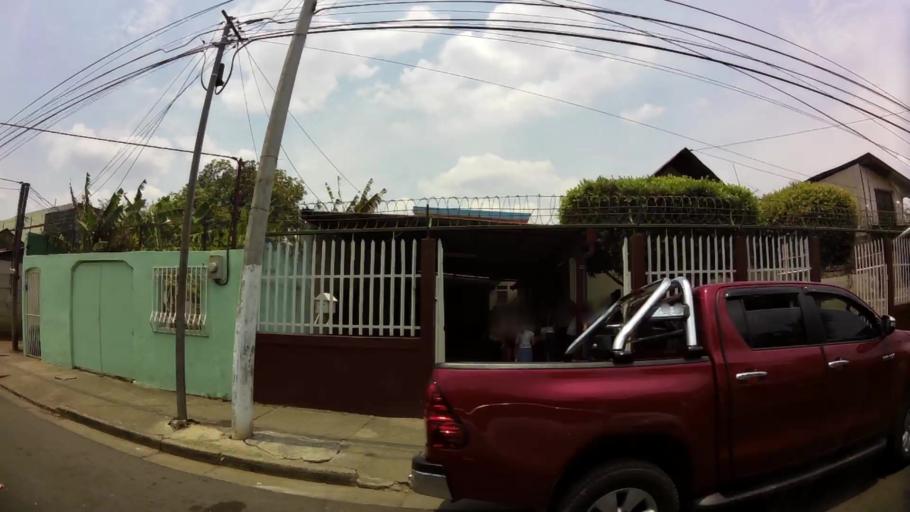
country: NI
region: Managua
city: Managua
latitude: 12.1322
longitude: -86.2963
